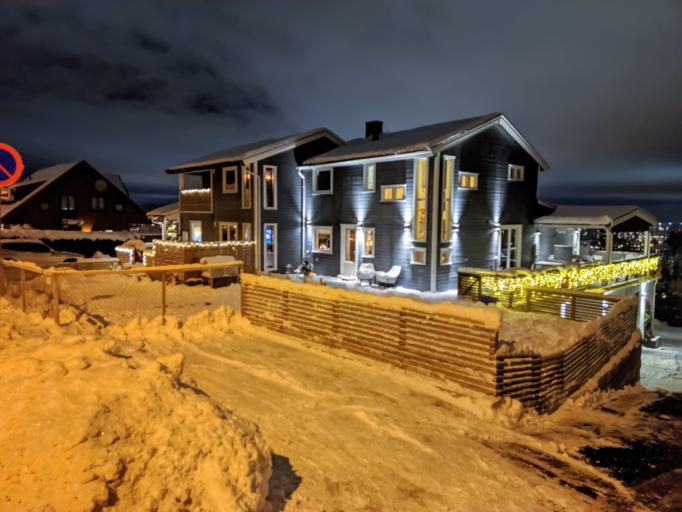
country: NO
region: Akershus
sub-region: Lorenskog
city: Kjenn
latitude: 59.9213
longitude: 10.9317
